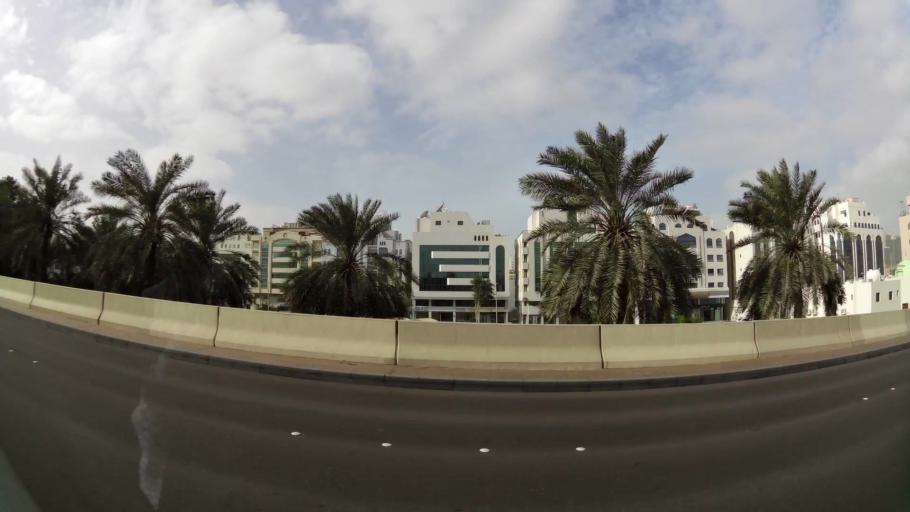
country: AE
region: Abu Dhabi
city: Abu Dhabi
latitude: 24.4673
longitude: 54.3810
